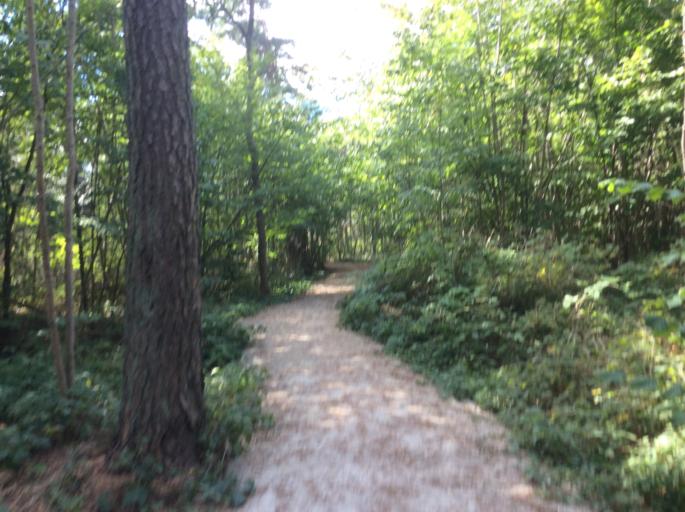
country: SE
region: Gotland
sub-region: Gotland
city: Vibble
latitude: 57.6188
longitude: 18.2687
